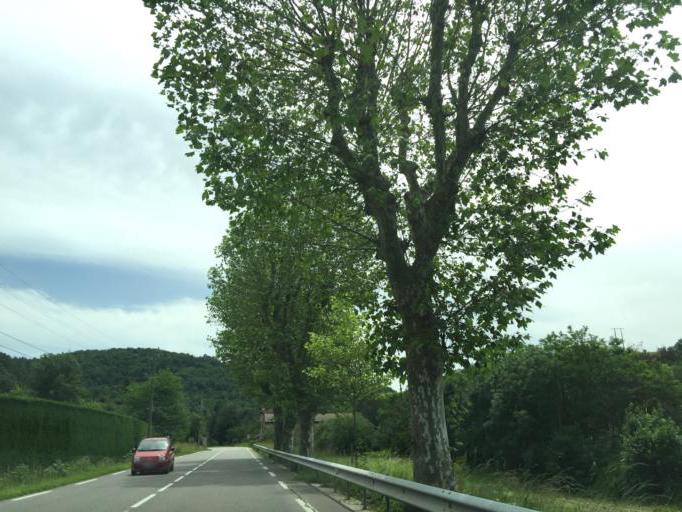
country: FR
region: Rhone-Alpes
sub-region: Departement de l'Ardeche
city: Saint-Marcel-les-Annonay
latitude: 45.2926
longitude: 4.6212
